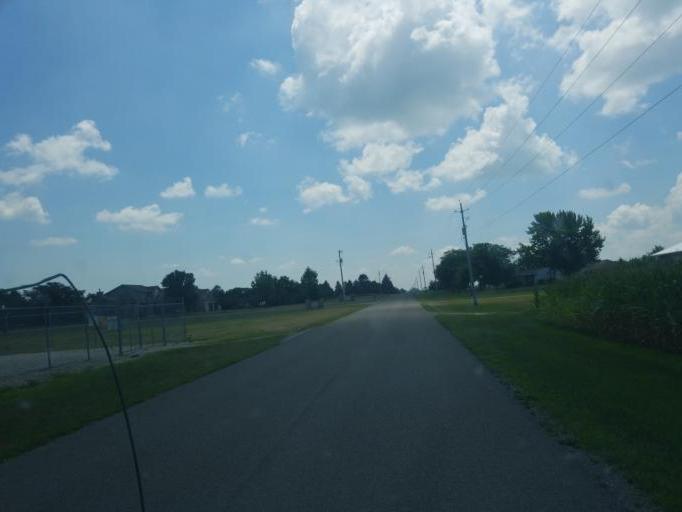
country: US
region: Ohio
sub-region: Mercer County
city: Celina
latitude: 40.5754
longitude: -84.4939
